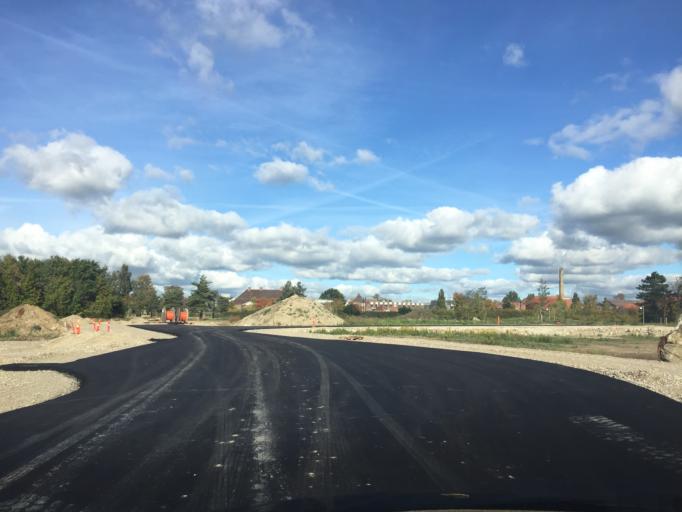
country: DK
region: Capital Region
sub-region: Hoje-Taastrup Kommune
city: Flong
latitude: 55.6470
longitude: 12.1967
